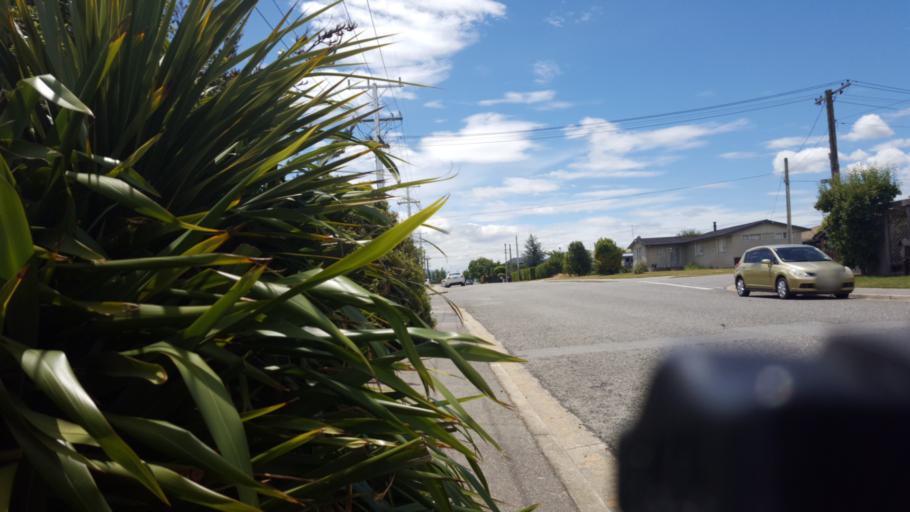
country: NZ
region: Otago
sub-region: Queenstown-Lakes District
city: Wanaka
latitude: -45.0441
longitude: 169.2112
